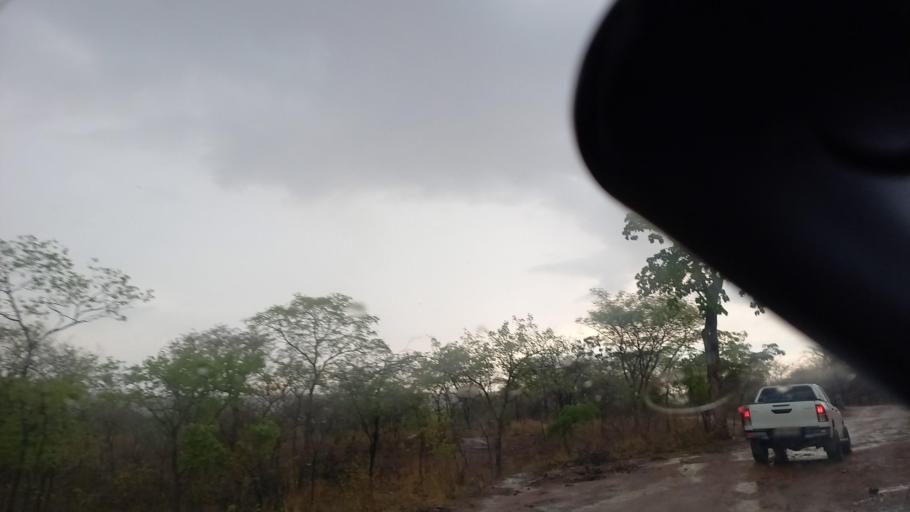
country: ZM
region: Lusaka
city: Kafue
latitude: -15.9461
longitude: 28.2196
